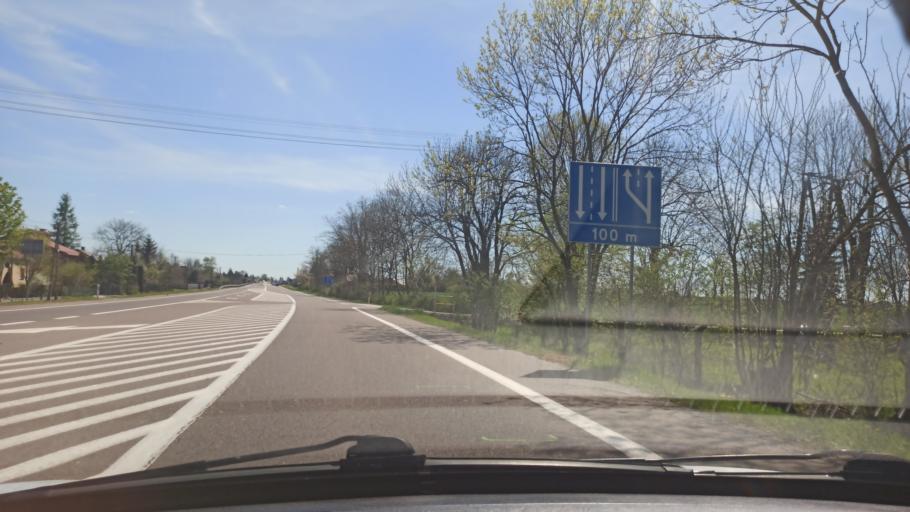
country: PL
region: Subcarpathian Voivodeship
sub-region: Powiat przemyski
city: Orly
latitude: 49.9004
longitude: 22.8158
